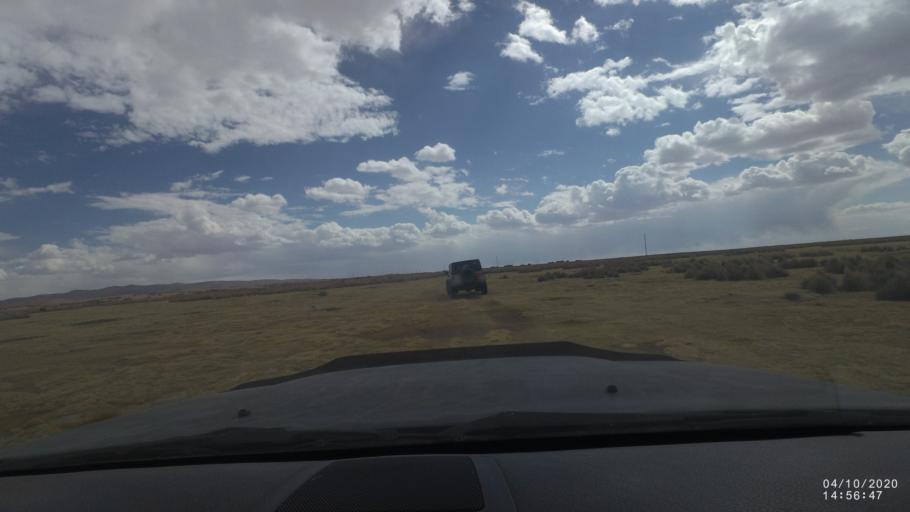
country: BO
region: Oruro
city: Poopo
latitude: -18.6849
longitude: -67.5172
